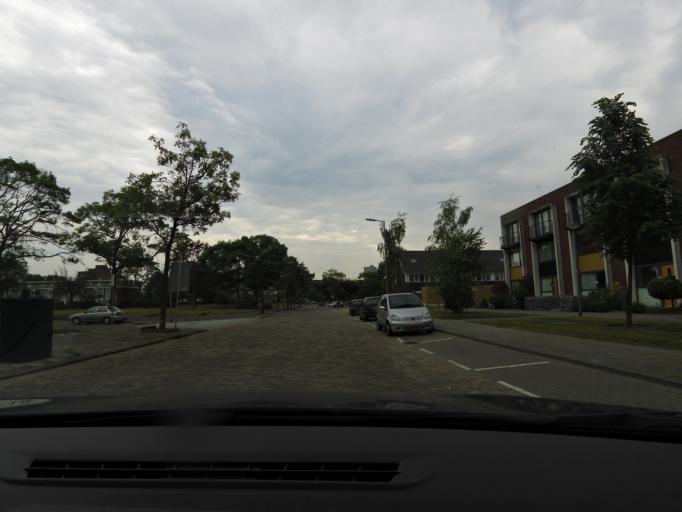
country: NL
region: South Holland
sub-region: Gemeente Spijkenisse
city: Spijkenisse
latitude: 51.8700
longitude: 4.3600
